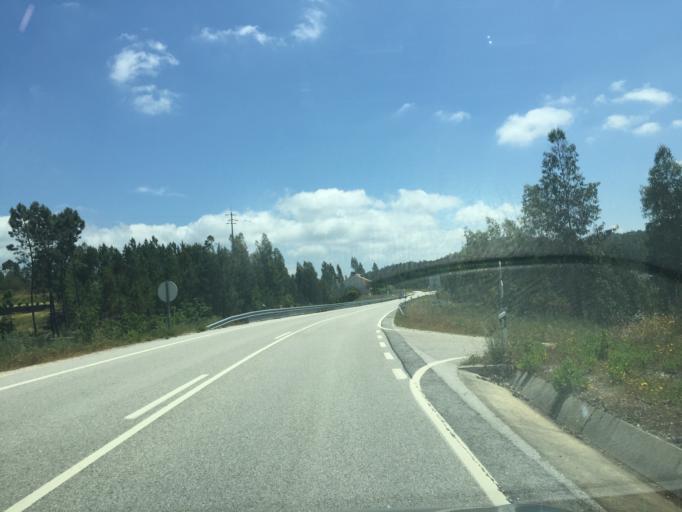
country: PT
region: Castelo Branco
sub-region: Vila de Rei
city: Vila de Rei
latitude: 39.7070
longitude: -8.1294
